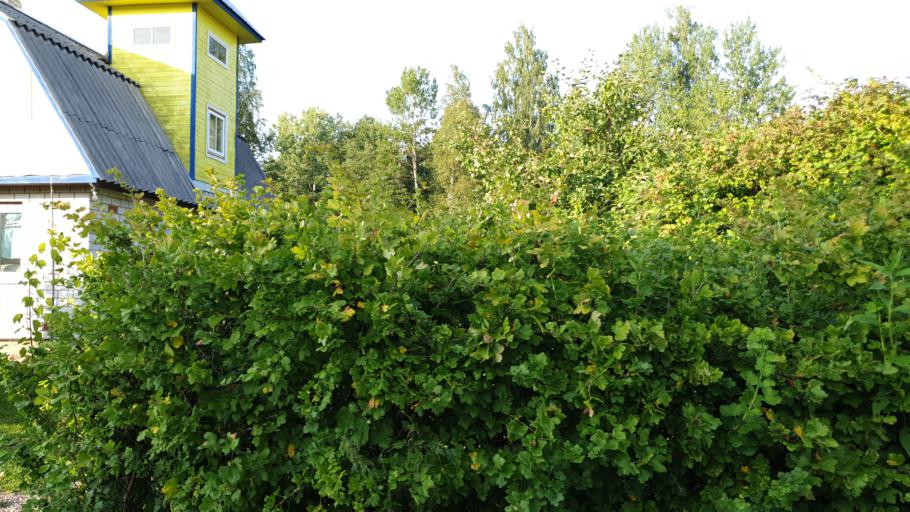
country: RU
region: Leningrad
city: Ivangorod
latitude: 59.4237
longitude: 28.3333
